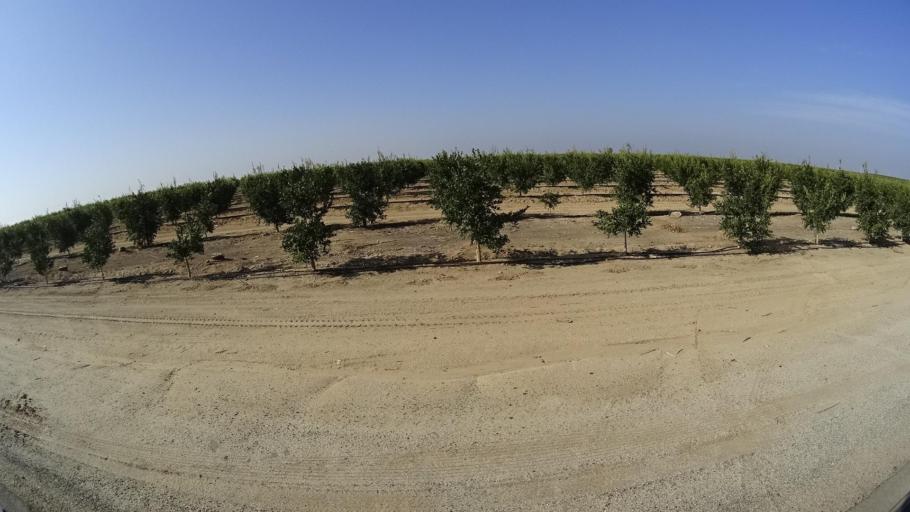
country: US
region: California
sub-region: Kern County
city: McFarland
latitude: 35.6045
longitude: -119.1688
